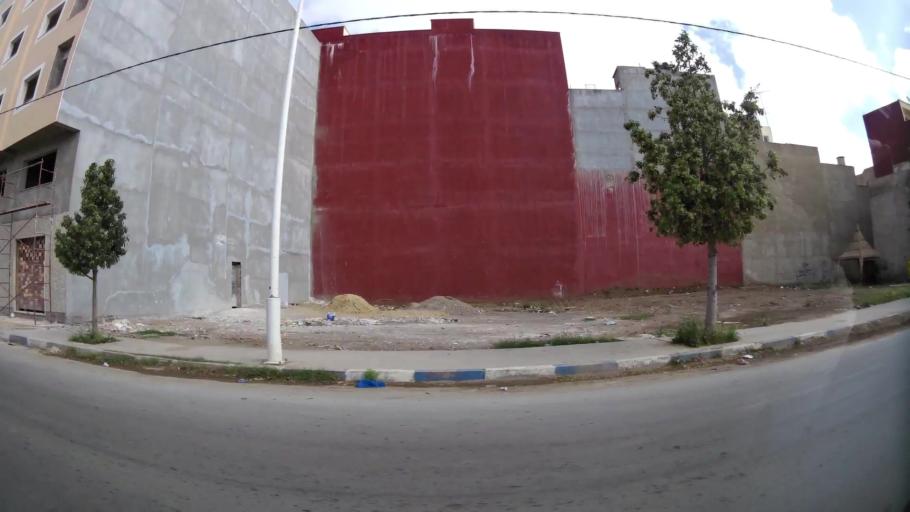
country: MA
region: Oriental
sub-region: Nador
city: Nador
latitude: 35.1614
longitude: -2.9266
